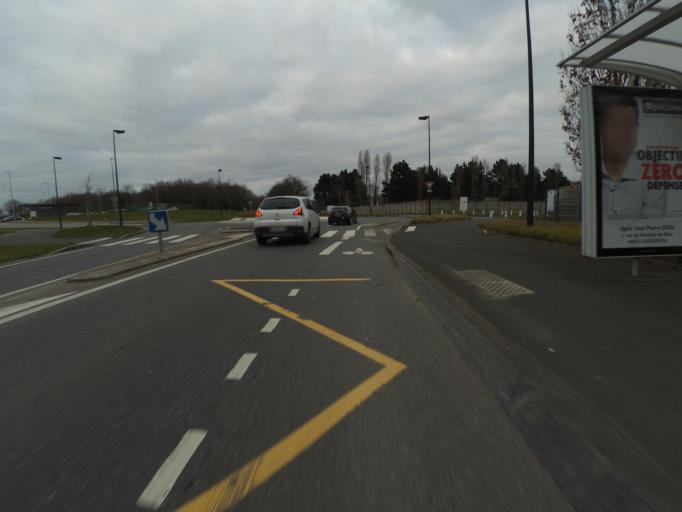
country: FR
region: Pays de la Loire
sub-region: Departement de la Loire-Atlantique
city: Sainte-Luce-sur-Loire
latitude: 47.2664
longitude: -1.5034
